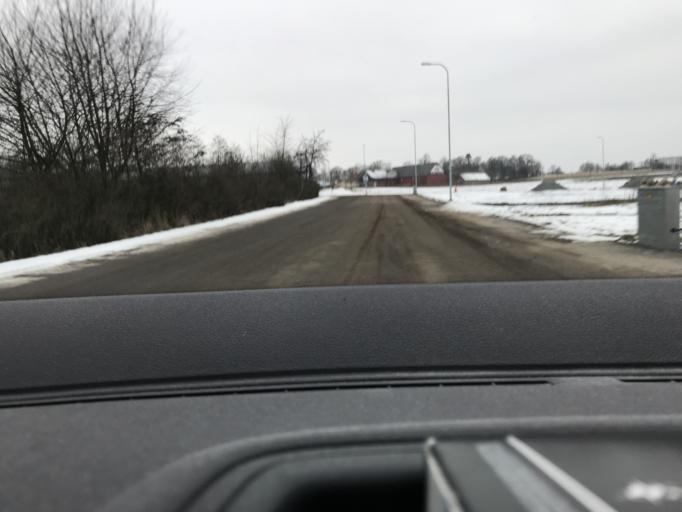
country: SE
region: Skane
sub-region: Ystads Kommun
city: Ystad
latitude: 55.4508
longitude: 13.8515
